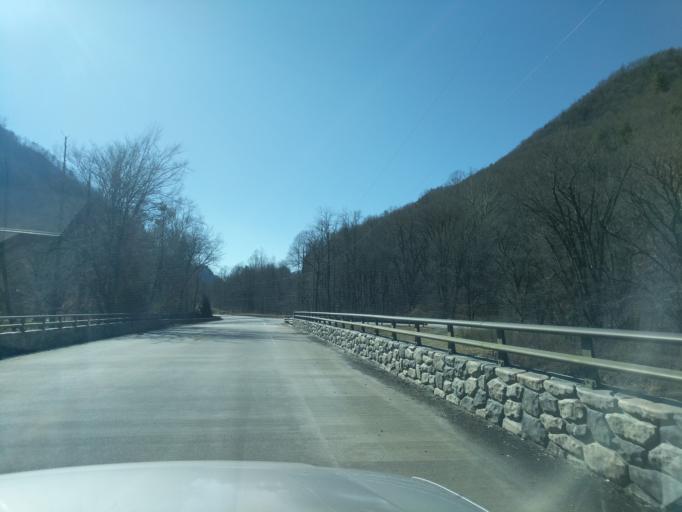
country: US
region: North Carolina
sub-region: Graham County
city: Robbinsville
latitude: 35.3019
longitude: -83.6535
